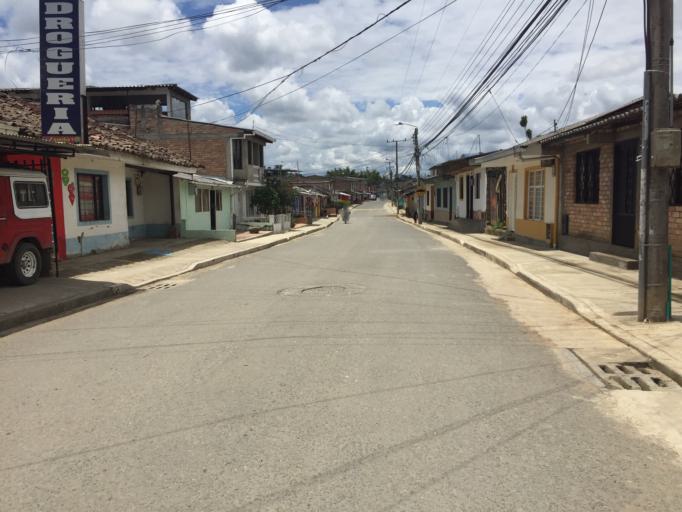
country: CO
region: Cauca
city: Popayan
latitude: 2.4552
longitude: -76.5864
